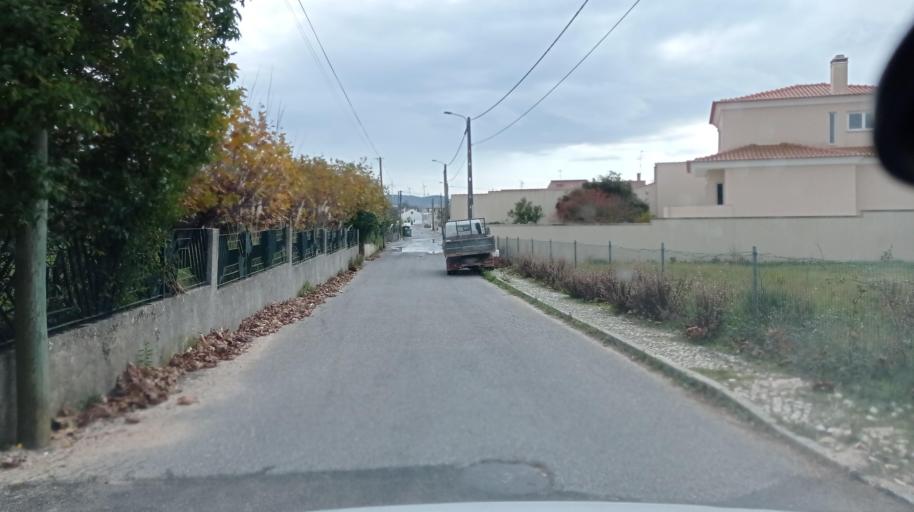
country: PT
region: Leiria
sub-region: Alcobaca
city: Benedita
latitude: 39.4239
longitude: -8.9763
